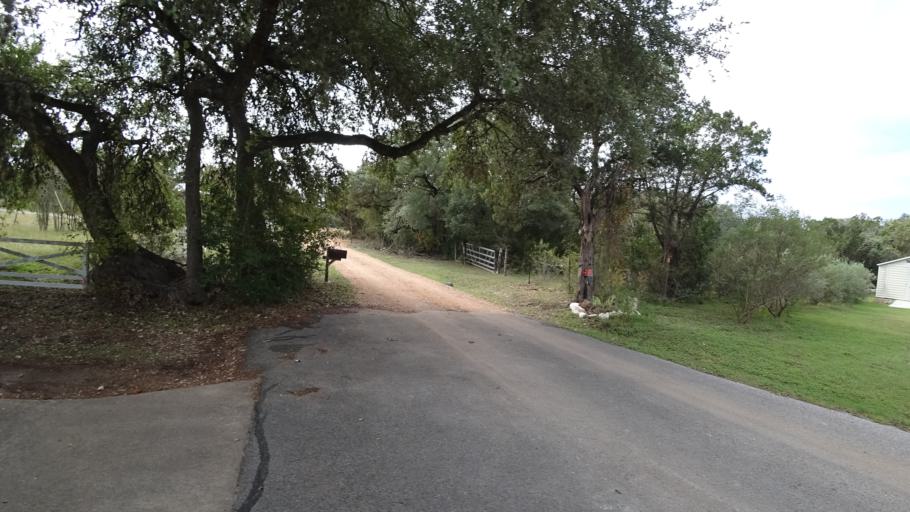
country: US
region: Texas
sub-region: Travis County
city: Shady Hollow
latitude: 30.1327
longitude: -97.8872
